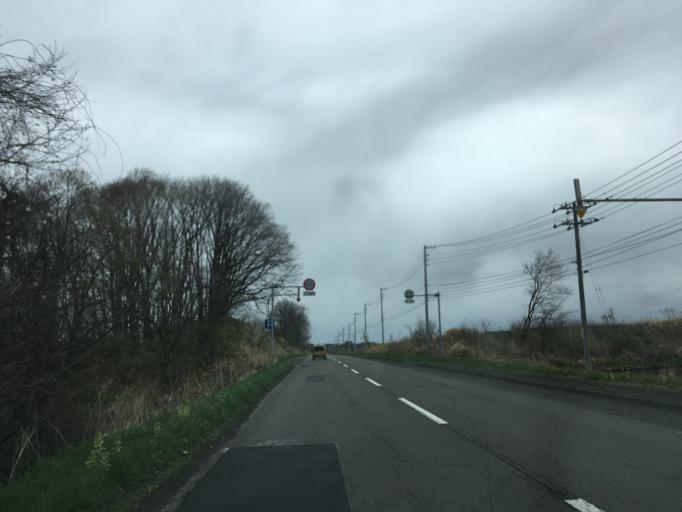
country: JP
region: Hokkaido
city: Chitose
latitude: 42.9008
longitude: 141.8135
